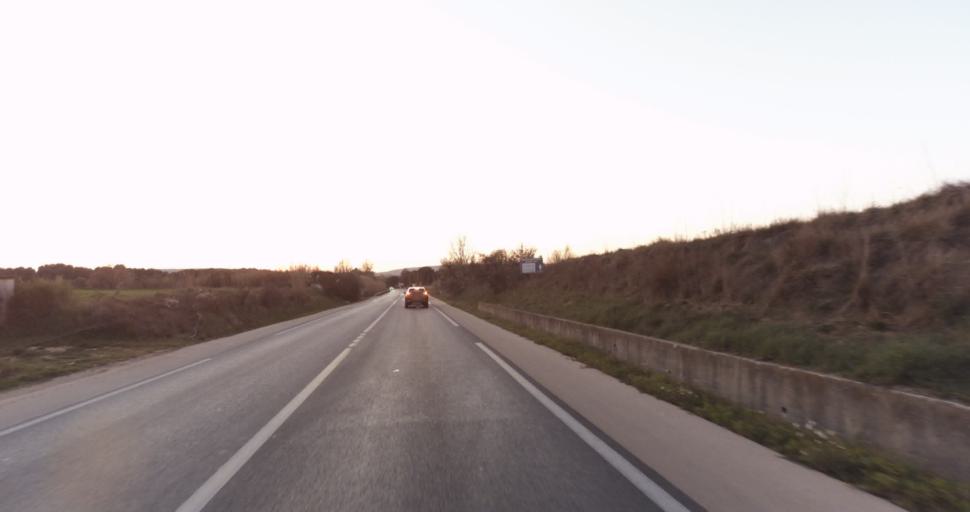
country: FR
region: Provence-Alpes-Cote d'Azur
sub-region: Departement des Bouches-du-Rhone
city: Eguilles
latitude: 43.5409
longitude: 5.3751
